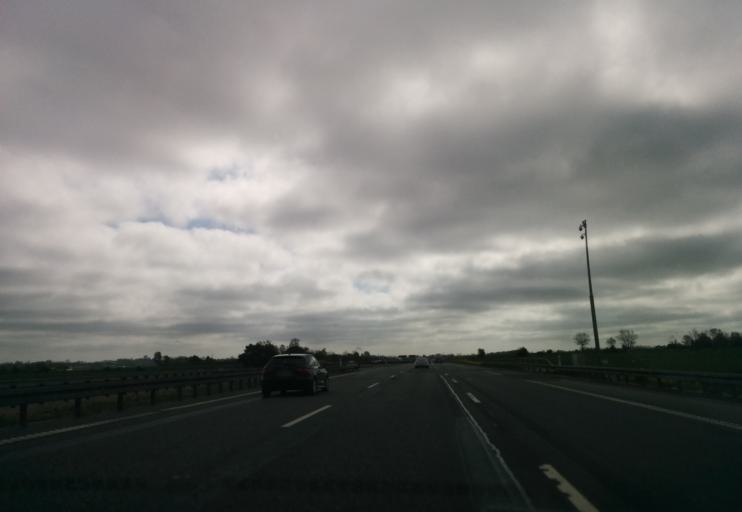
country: DK
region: South Denmark
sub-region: Middelfart Kommune
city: Norre Aby
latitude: 55.4894
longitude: 9.8350
